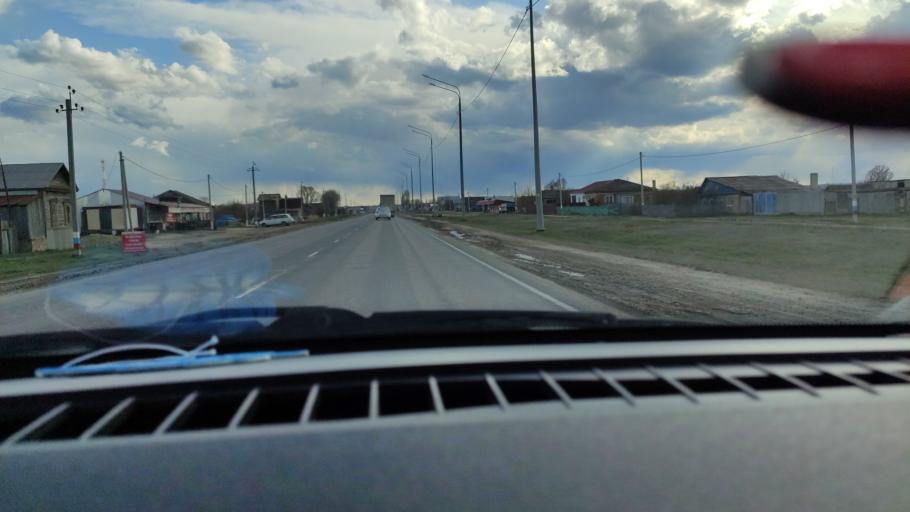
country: RU
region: Saratov
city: Sinodskoye
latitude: 51.9864
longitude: 46.6640
